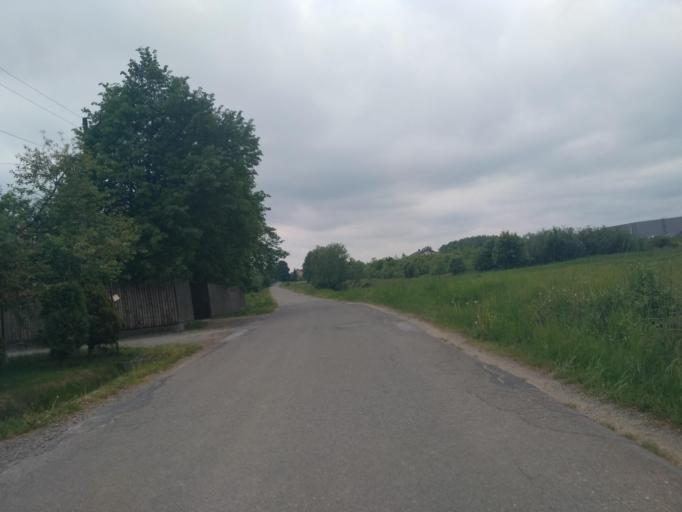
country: PL
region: Subcarpathian Voivodeship
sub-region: Krosno
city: Krosno
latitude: 49.6724
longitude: 21.7418
